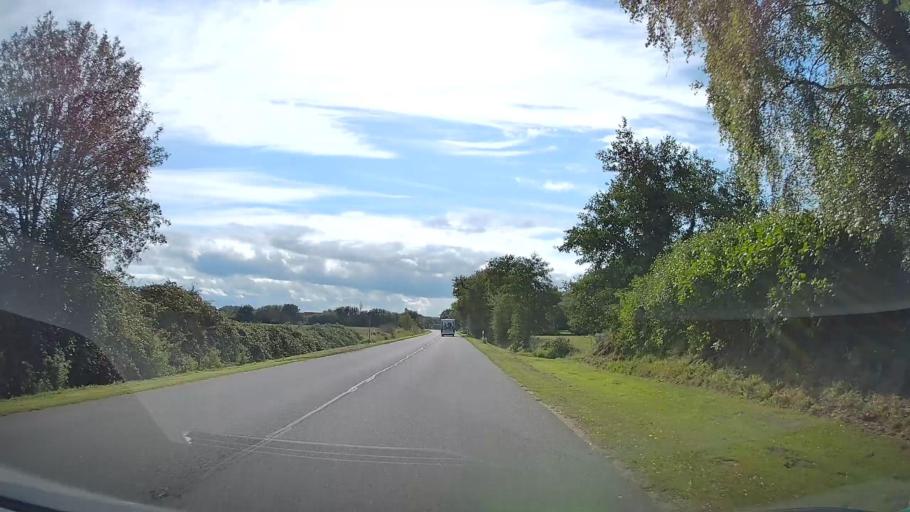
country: DE
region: Schleswig-Holstein
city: Glucksburg
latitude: 54.8646
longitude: 9.5924
